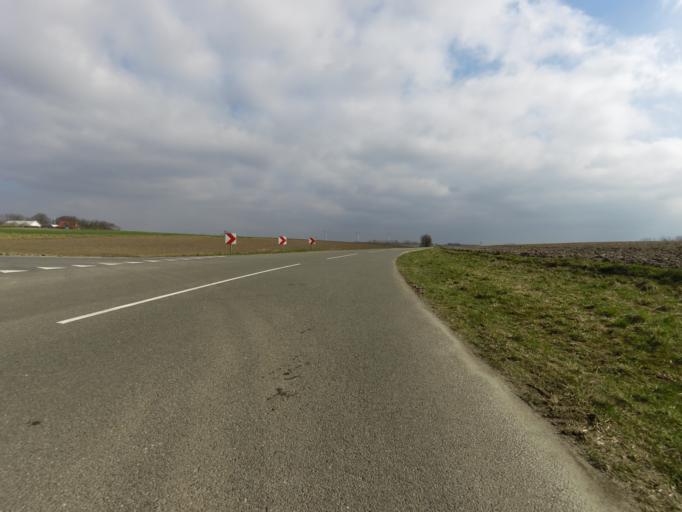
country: DK
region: Central Jutland
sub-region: Holstebro Kommune
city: Holstebro
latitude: 56.4367
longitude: 8.6689
